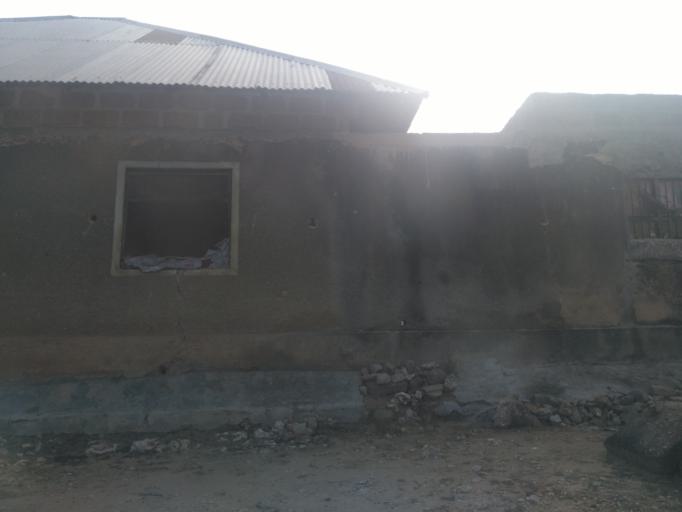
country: TZ
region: Zanzibar Urban/West
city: Zanzibar
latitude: -6.1555
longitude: 39.2111
